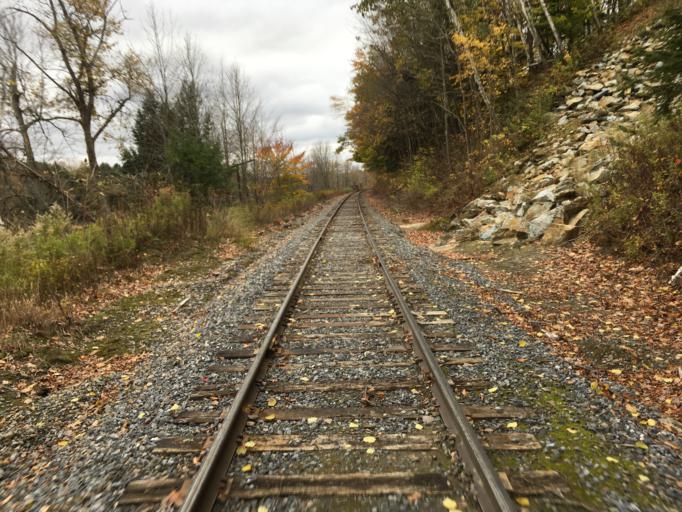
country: US
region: New Hampshire
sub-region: Grafton County
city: Woodsville
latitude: 44.1739
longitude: -72.0555
